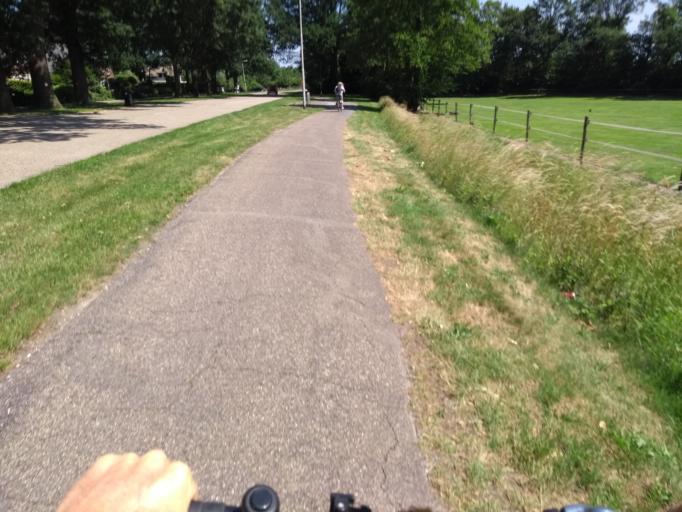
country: NL
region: Overijssel
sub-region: Gemeente Wierden
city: Wierden
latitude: 52.3563
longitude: 6.6111
